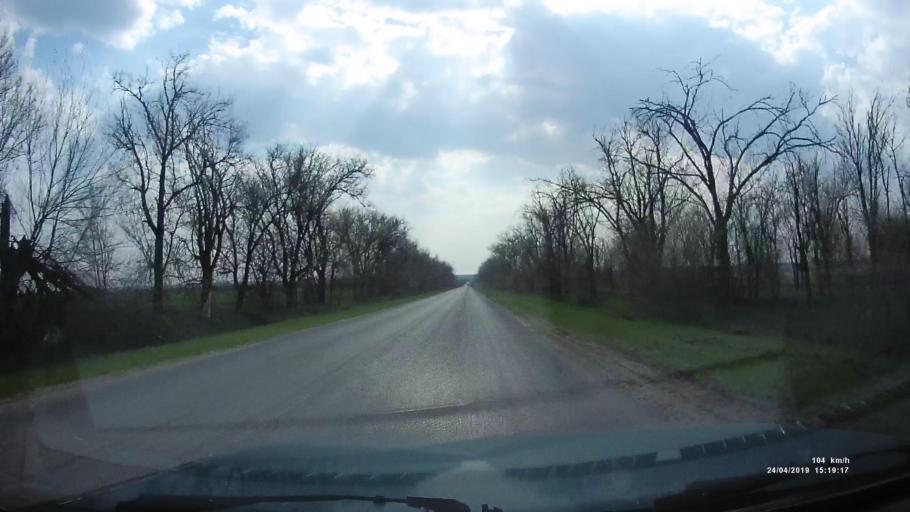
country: RU
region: Rostov
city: Remontnoye
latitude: 46.5411
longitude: 43.1494
